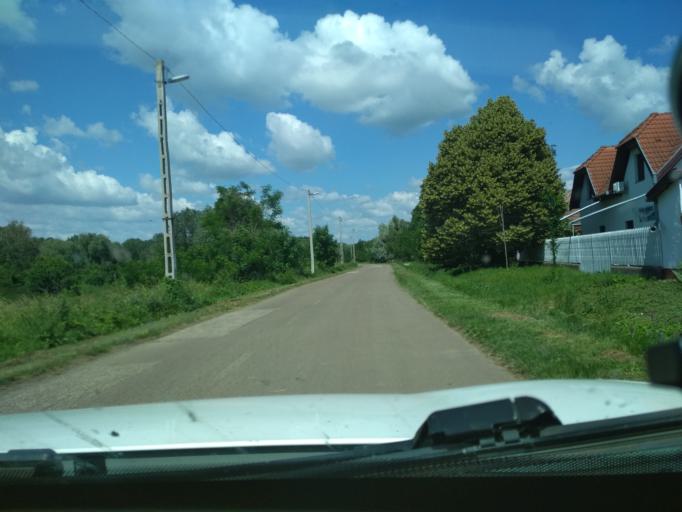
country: HU
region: Jasz-Nagykun-Szolnok
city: Abadszalok
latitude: 47.4819
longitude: 20.5936
